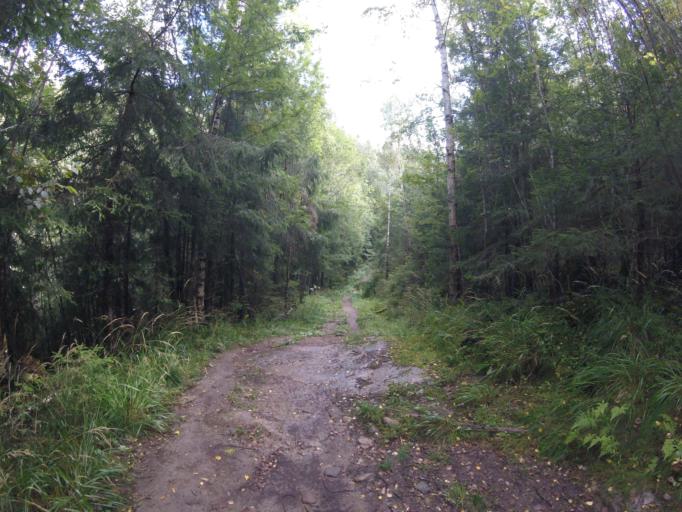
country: NO
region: Akershus
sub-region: Raelingen
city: Fjerdingby
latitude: 59.9158
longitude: 11.0333
